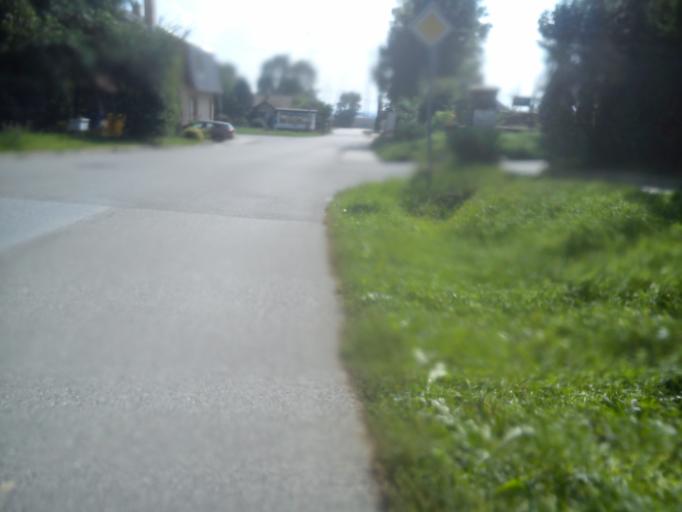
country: CZ
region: South Moravian
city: Sokolnice
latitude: 49.1095
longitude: 16.7296
